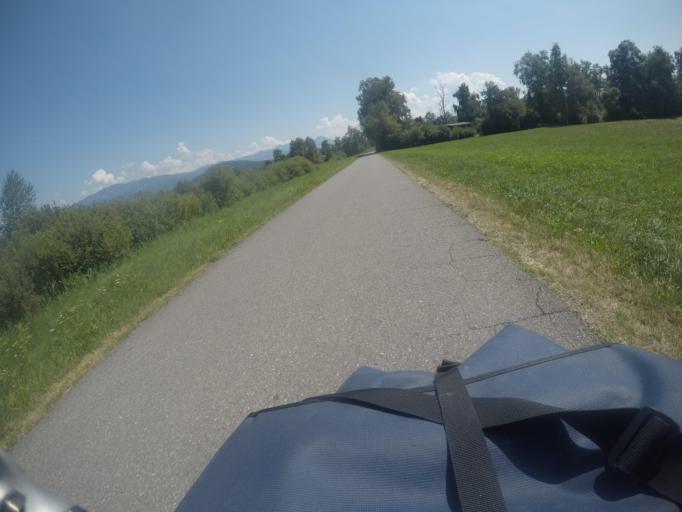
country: AT
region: Vorarlberg
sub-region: Politischer Bezirk Feldkirch
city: Koblach
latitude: 47.3545
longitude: 9.5752
